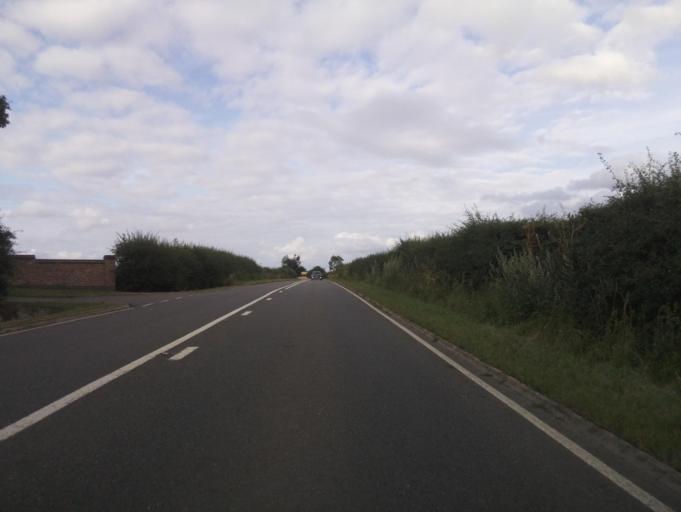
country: GB
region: England
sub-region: Warwickshire
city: Dunchurch
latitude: 52.3205
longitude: -1.3083
